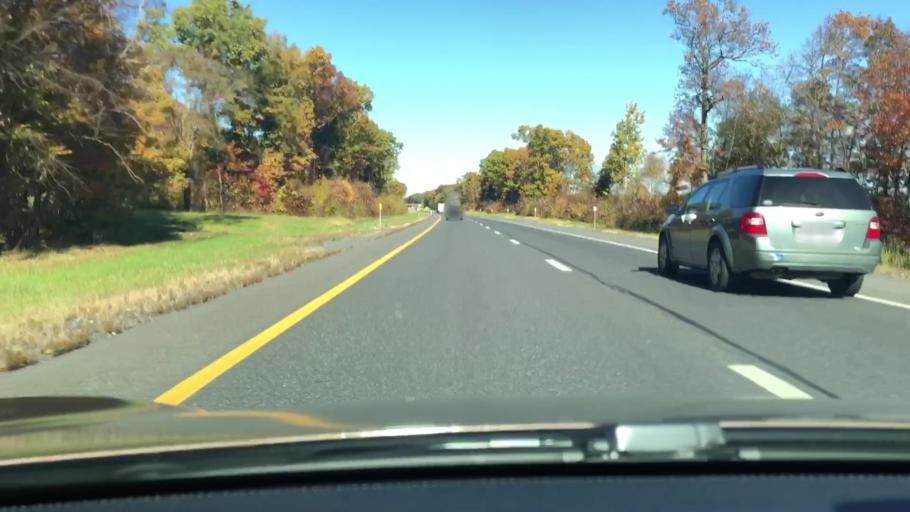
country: US
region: New York
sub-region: Ulster County
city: New Paltz
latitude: 41.7590
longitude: -74.0566
